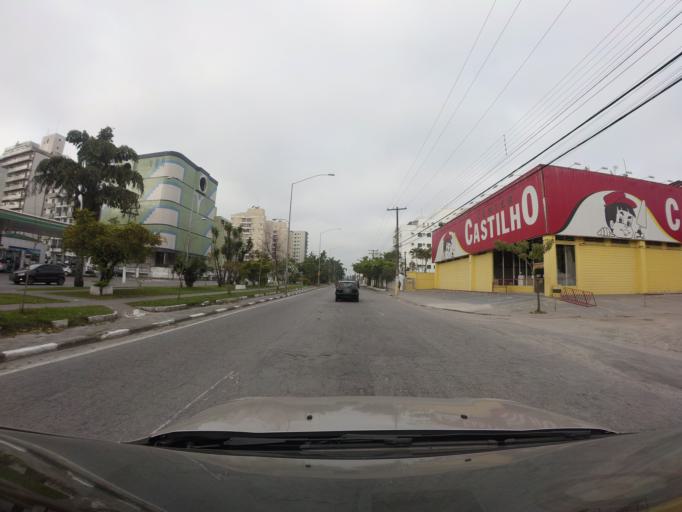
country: BR
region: Sao Paulo
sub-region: Guaruja
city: Guaruja
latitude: -23.9861
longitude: -46.2426
